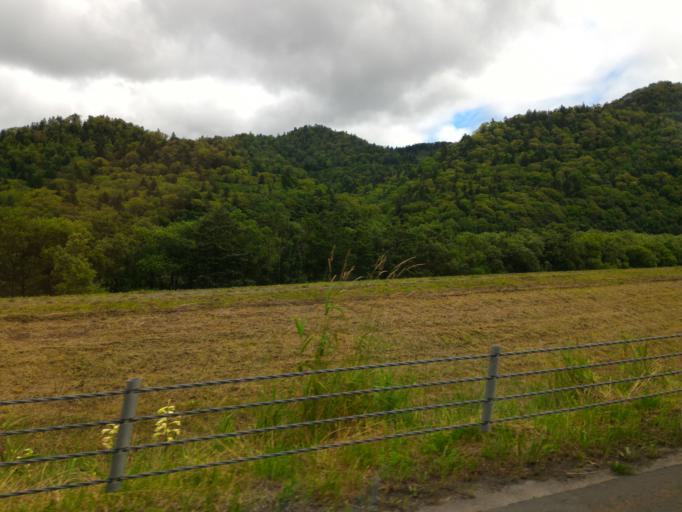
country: JP
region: Hokkaido
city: Nayoro
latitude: 44.7311
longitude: 142.2081
